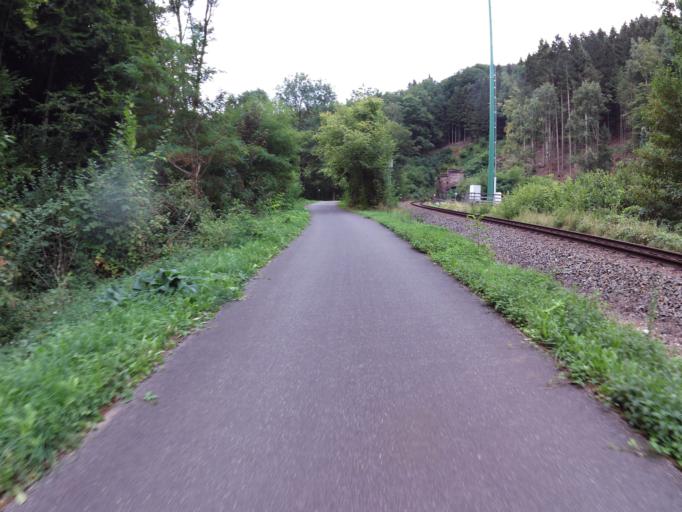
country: DE
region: Rheinland-Pfalz
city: Kyllburg
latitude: 50.0501
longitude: 6.6006
